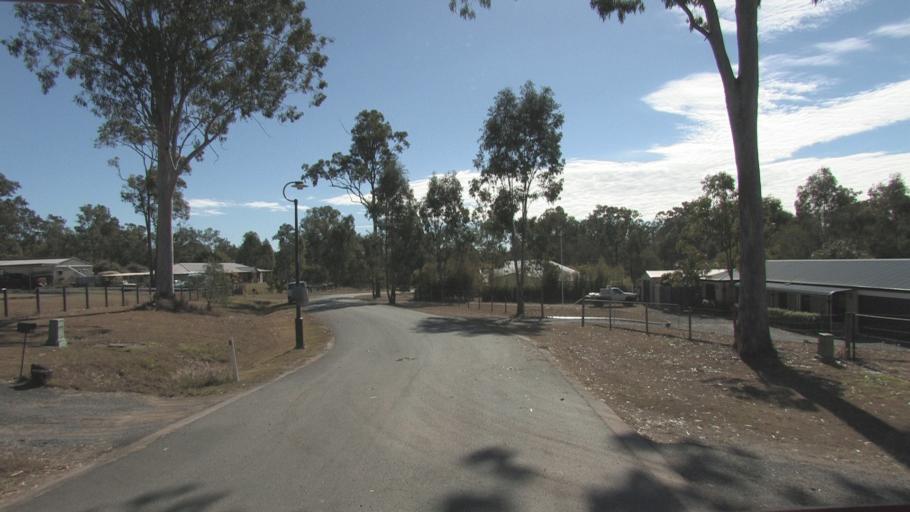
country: AU
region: Queensland
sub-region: Logan
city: North Maclean
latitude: -27.7999
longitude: 153.0443
